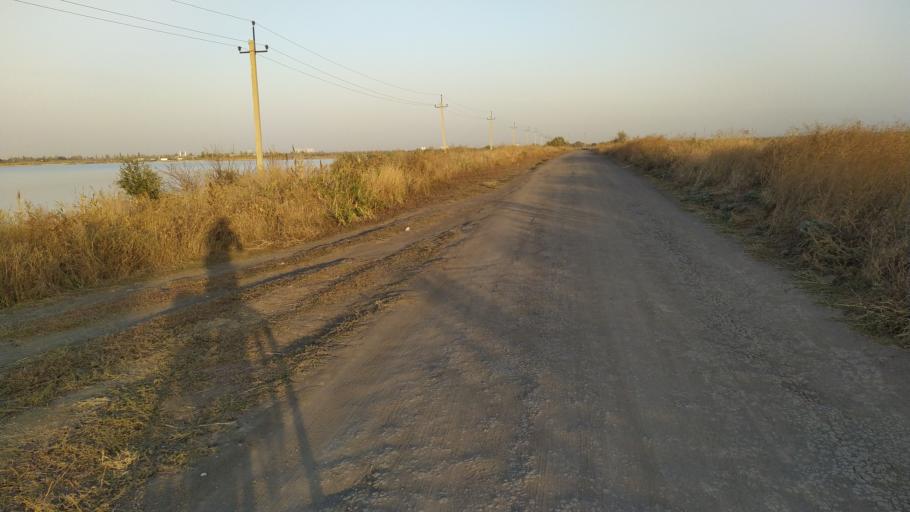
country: RU
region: Rostov
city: Bataysk
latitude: 47.1378
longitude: 39.6469
